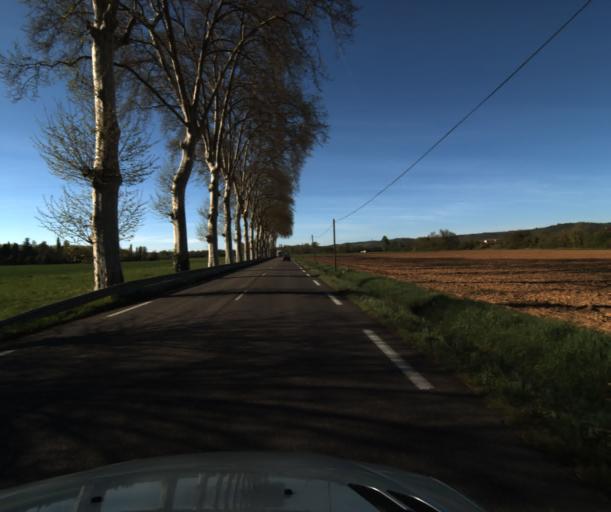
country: FR
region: Midi-Pyrenees
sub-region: Departement du Tarn-et-Garonne
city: Lafrancaise
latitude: 44.0779
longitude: 1.2811
